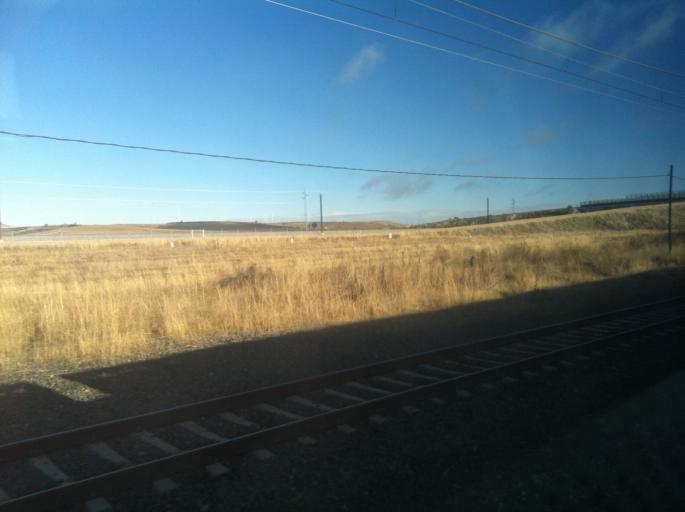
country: ES
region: Castille and Leon
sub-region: Provincia de Palencia
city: Villodrigo
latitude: 42.1480
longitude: -4.1047
